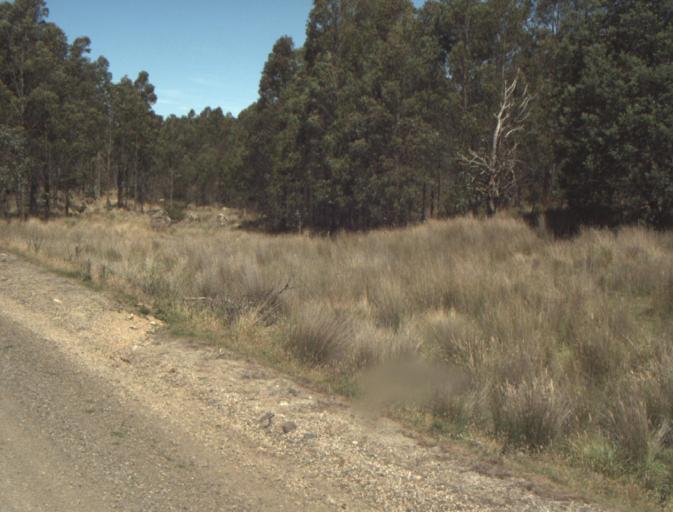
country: AU
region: Tasmania
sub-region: Dorset
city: Scottsdale
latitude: -41.3201
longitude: 147.4554
